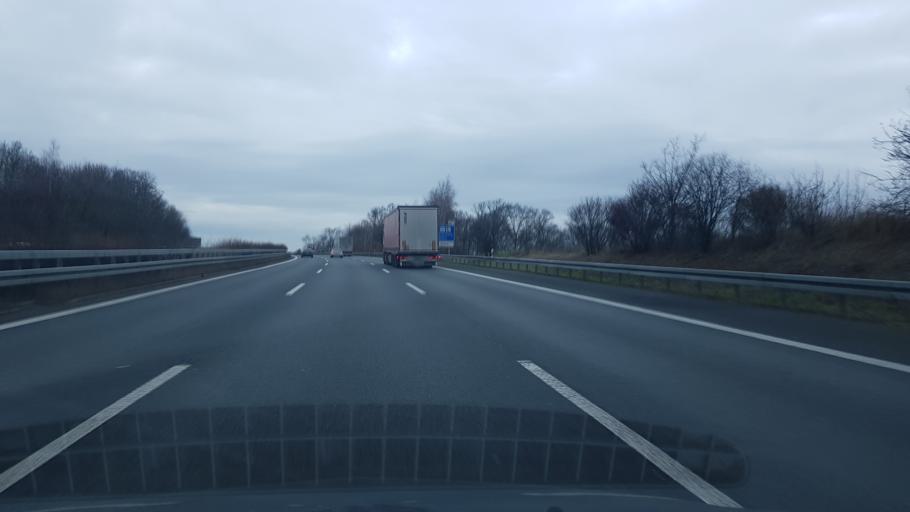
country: DE
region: Saxony
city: Nossen
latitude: 51.0471
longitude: 13.3418
